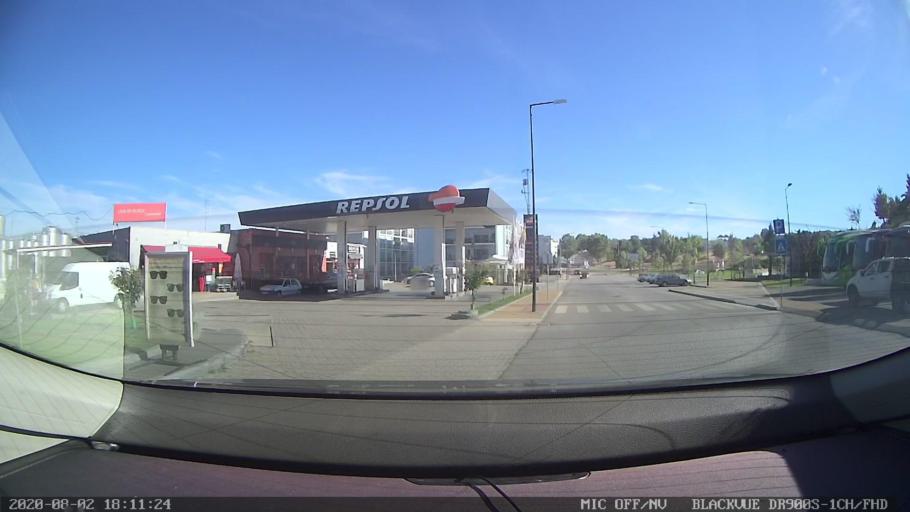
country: PT
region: Vila Real
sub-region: Murca
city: Murca
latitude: 41.4066
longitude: -7.4502
